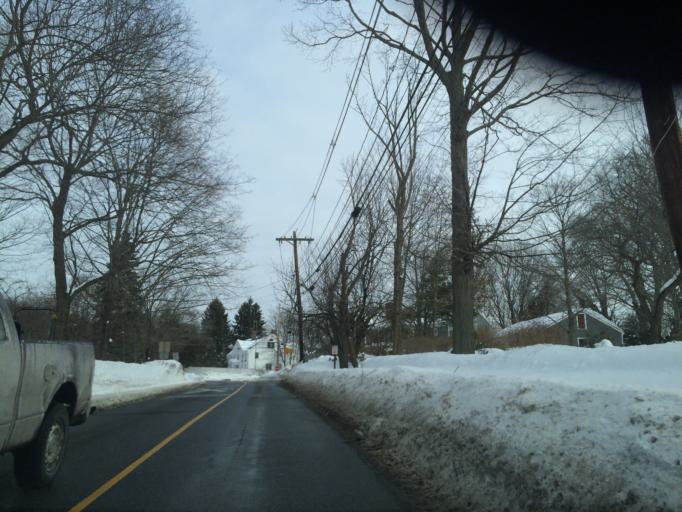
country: US
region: Massachusetts
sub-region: Middlesex County
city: Weston
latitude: 42.3791
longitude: -71.2822
